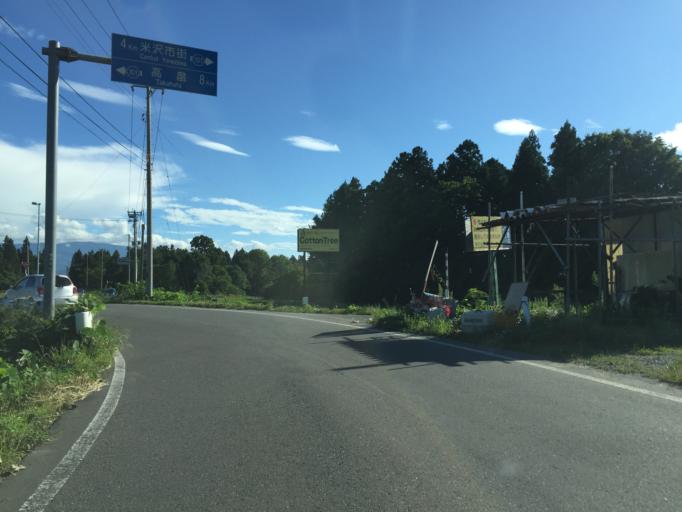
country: JP
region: Yamagata
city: Yonezawa
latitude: 37.9515
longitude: 140.1385
